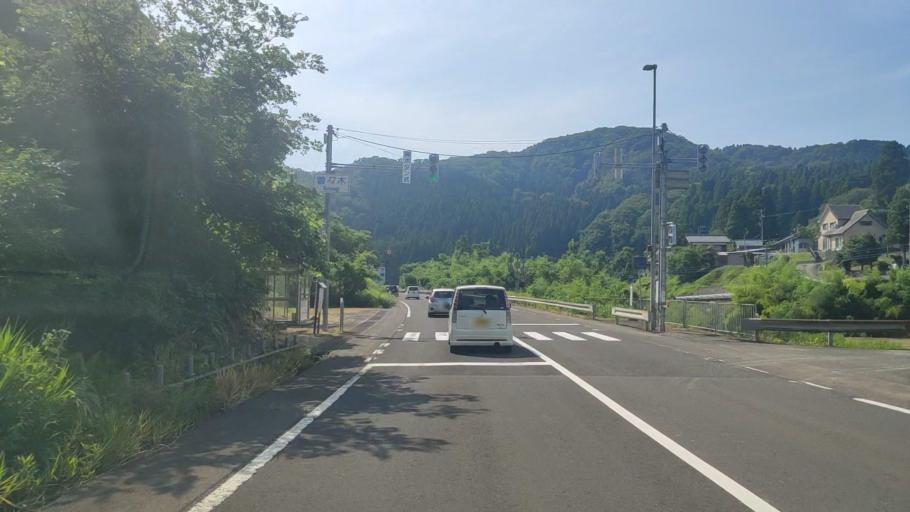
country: JP
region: Fukui
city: Tsuruga
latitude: 35.6092
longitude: 136.1180
